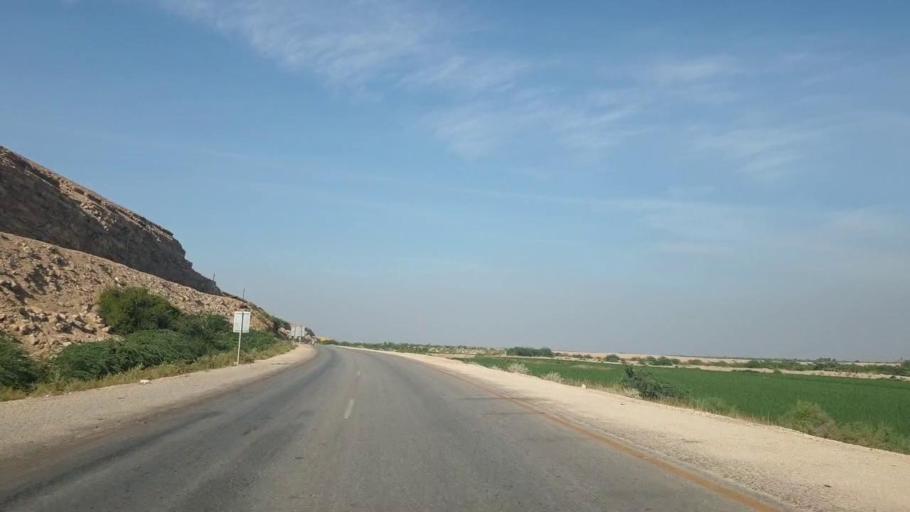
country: PK
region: Sindh
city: Sehwan
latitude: 26.3623
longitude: 67.8738
